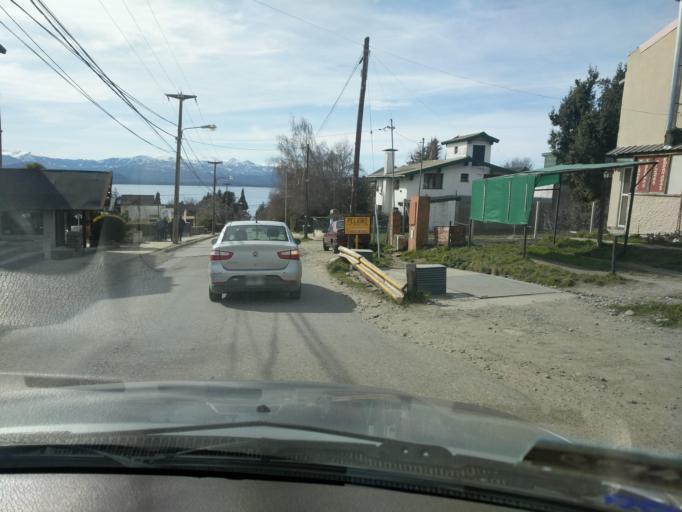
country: AR
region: Rio Negro
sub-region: Departamento de Bariloche
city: San Carlos de Bariloche
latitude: -41.1318
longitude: -71.3572
